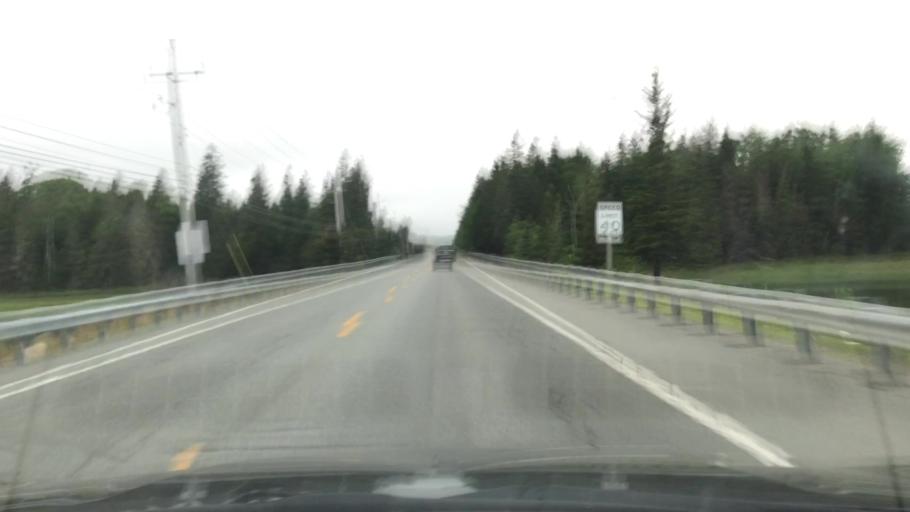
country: US
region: Maine
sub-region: Hancock County
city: Trenton
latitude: 44.4250
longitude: -68.3653
